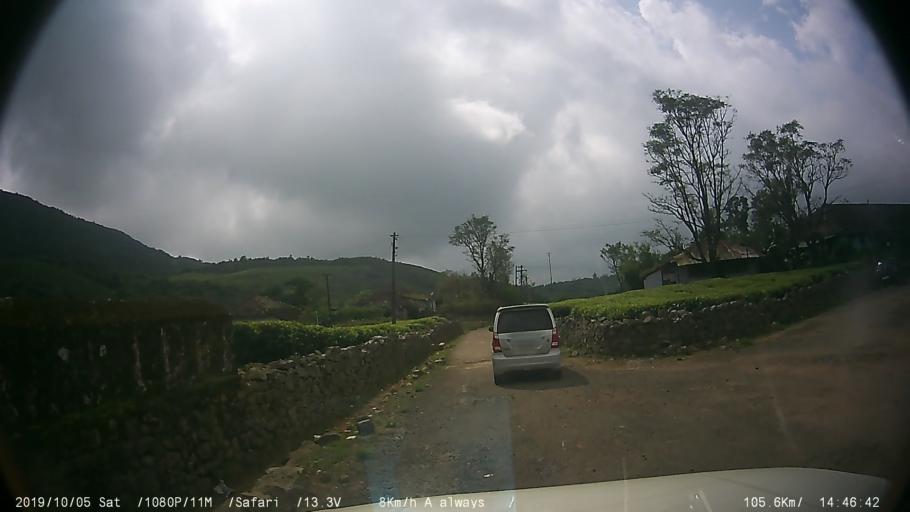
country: IN
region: Kerala
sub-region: Kottayam
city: Erattupetta
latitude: 9.6176
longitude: 76.9430
